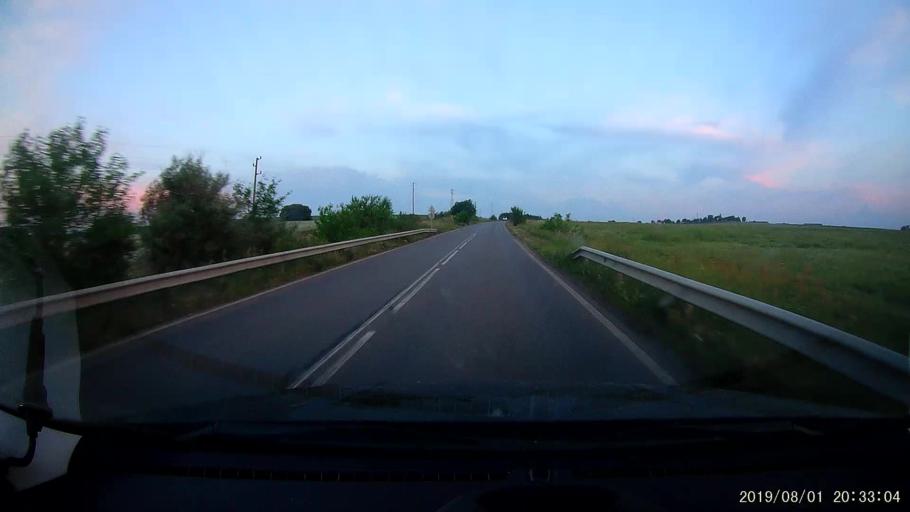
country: BG
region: Yambol
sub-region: Obshtina Elkhovo
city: Elkhovo
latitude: 42.1119
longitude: 26.5315
